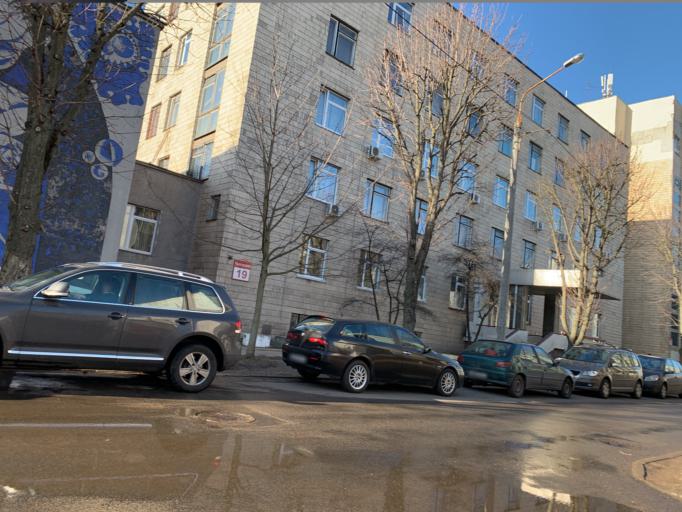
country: BY
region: Minsk
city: Minsk
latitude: 53.9146
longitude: 27.5656
